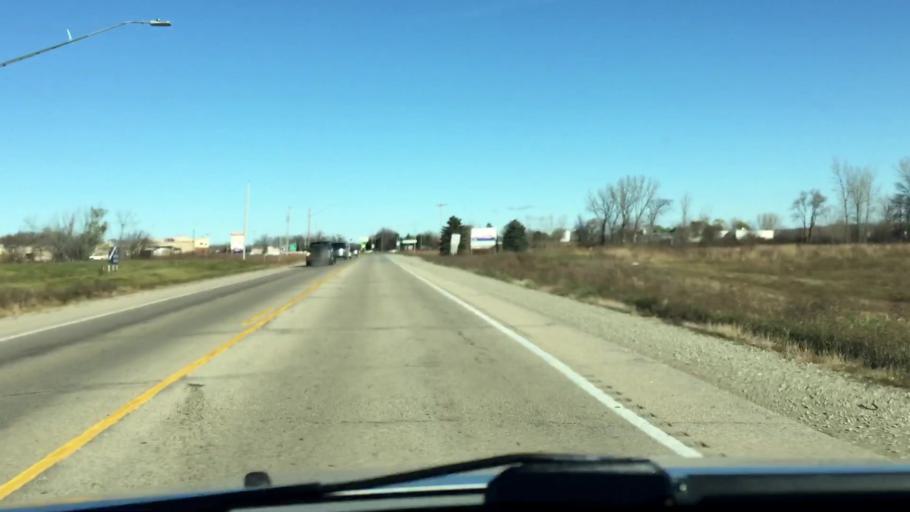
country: US
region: Wisconsin
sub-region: Brown County
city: Pulaski
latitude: 44.6522
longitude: -88.2204
